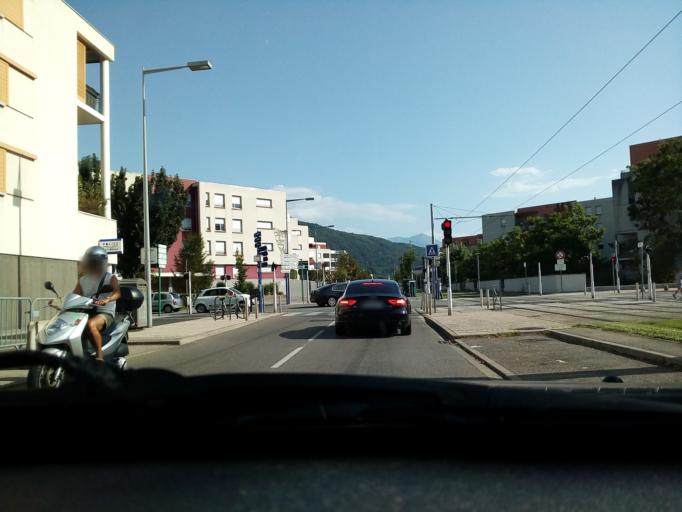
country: FR
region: Rhone-Alpes
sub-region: Departement de l'Isere
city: Saint-Martin-d'Heres
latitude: 45.1779
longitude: 5.7560
